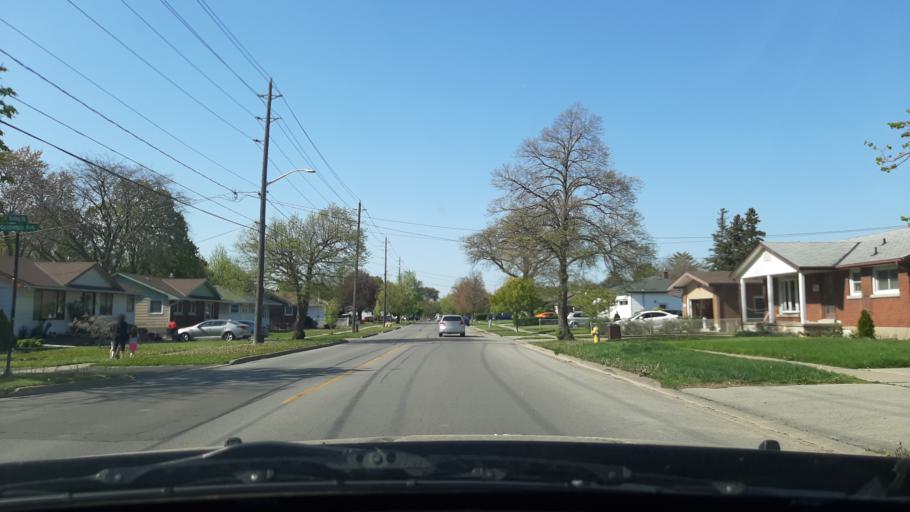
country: CA
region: Ontario
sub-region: Regional Municipality of Niagara
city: St. Catharines
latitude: 43.2003
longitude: -79.2113
